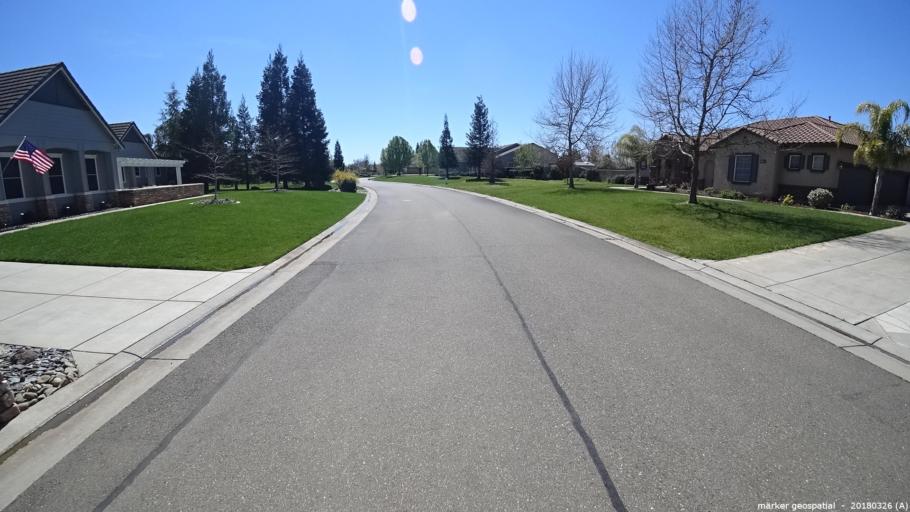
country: US
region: California
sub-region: Sacramento County
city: Vineyard
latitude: 38.4654
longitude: -121.2927
